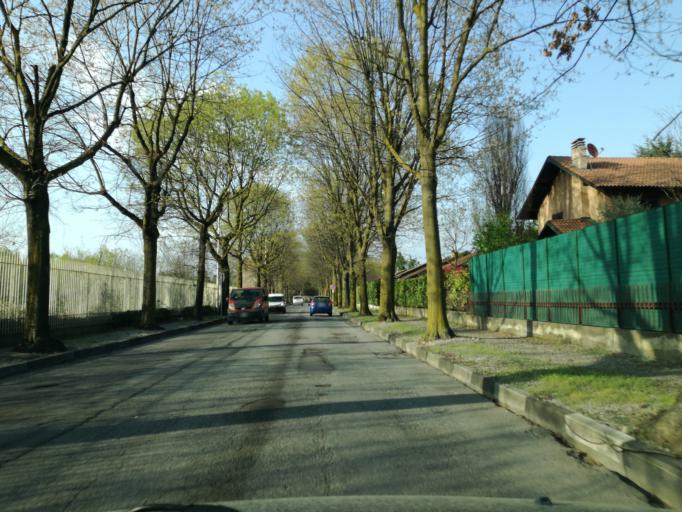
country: IT
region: Lombardy
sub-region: Provincia di Monza e Brianza
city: Carnate
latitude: 45.6451
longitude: 9.3733
